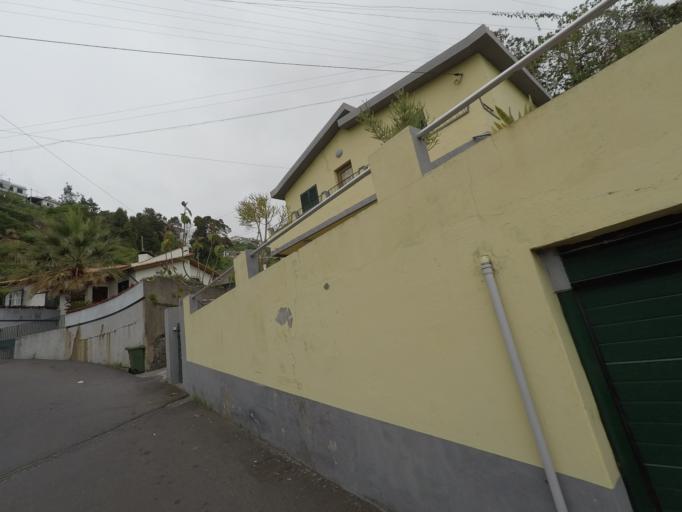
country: PT
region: Madeira
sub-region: Funchal
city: Nossa Senhora do Monte
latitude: 32.6721
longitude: -16.9369
